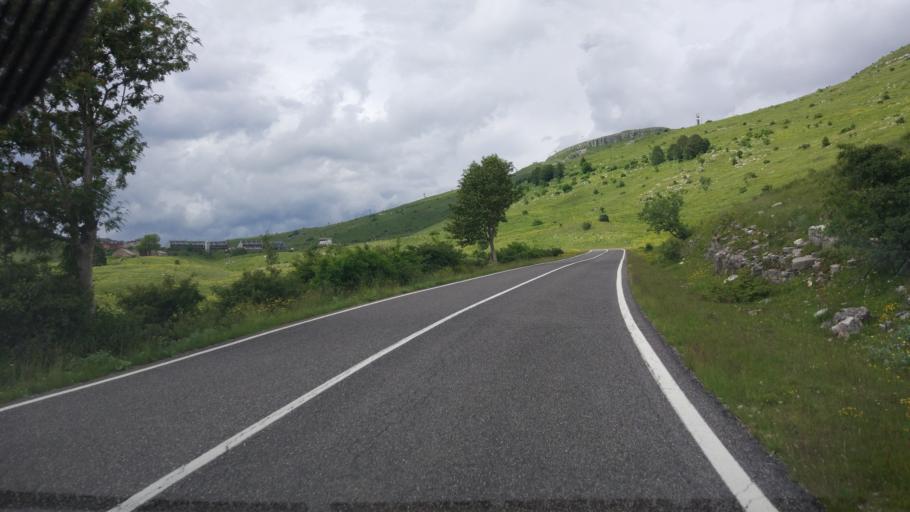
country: IT
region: Veneto
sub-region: Provincia di Verona
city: Velo Veronese
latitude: 45.6767
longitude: 11.0892
